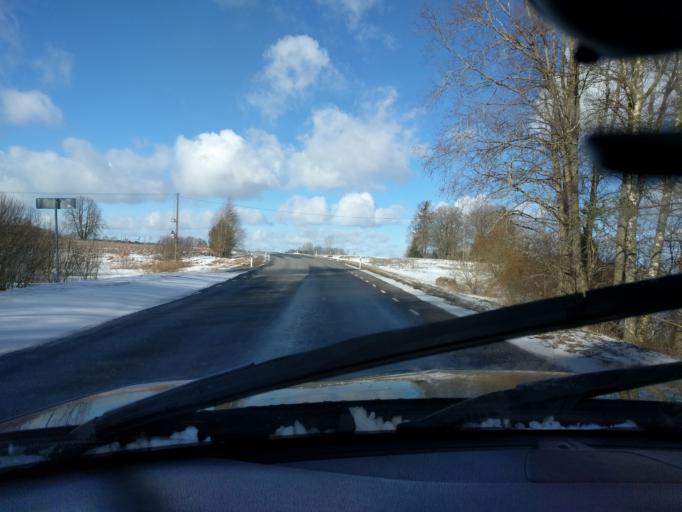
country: EE
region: Harju
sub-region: Anija vald
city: Kehra
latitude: 59.2407
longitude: 25.3685
